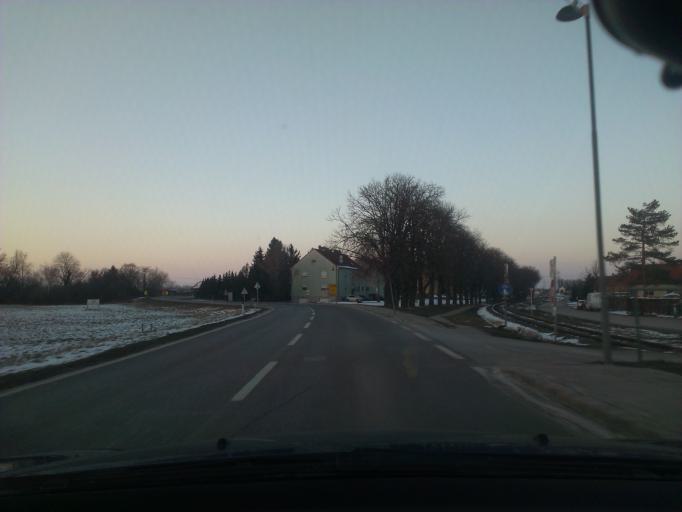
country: AT
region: Lower Austria
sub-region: Politischer Bezirk Bruck an der Leitha
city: Gotzendorf an der Leitha
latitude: 48.0162
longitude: 16.5826
